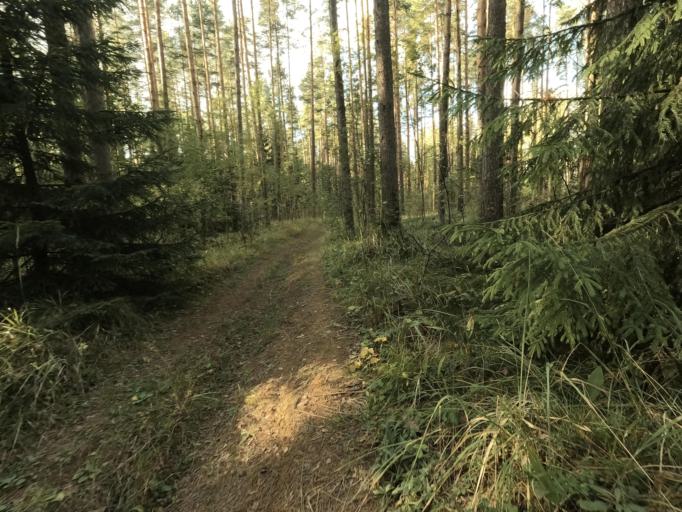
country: RU
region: Leningrad
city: Imeni Sverdlova
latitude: 59.8469
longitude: 30.7288
